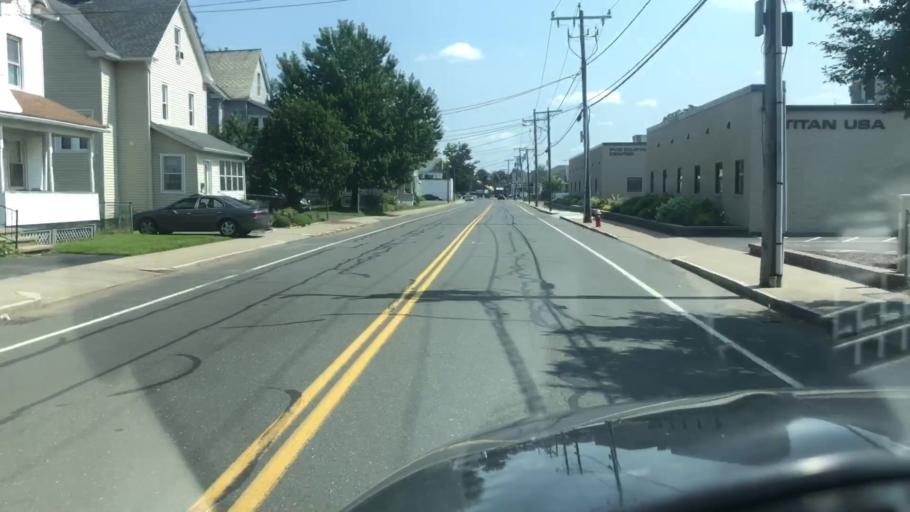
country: US
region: Massachusetts
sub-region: Hampden County
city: West Springfield
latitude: 42.0959
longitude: -72.6219
